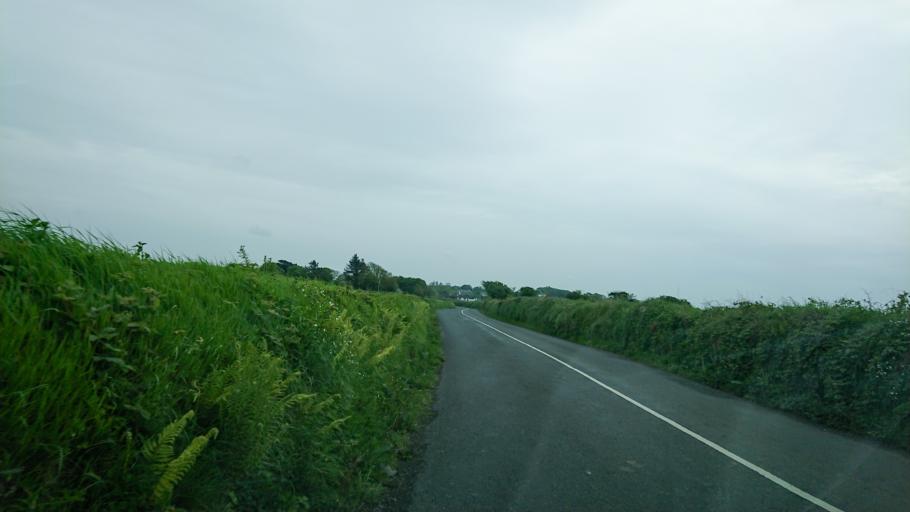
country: IE
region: Munster
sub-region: Waterford
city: Waterford
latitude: 52.2193
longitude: -7.0479
